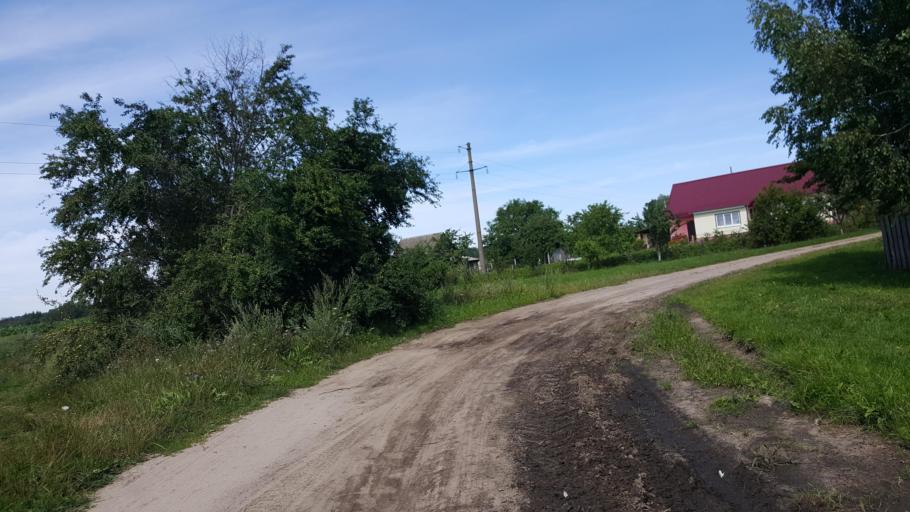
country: BY
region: Brest
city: Pruzhany
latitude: 52.5623
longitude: 24.2043
